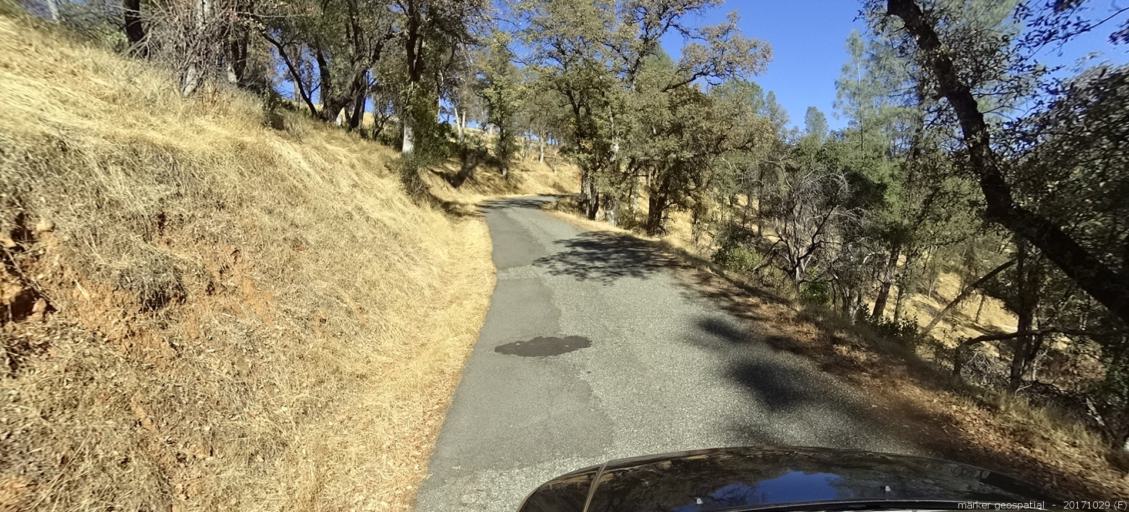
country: US
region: California
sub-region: Shasta County
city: Shasta
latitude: 40.4801
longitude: -122.6246
